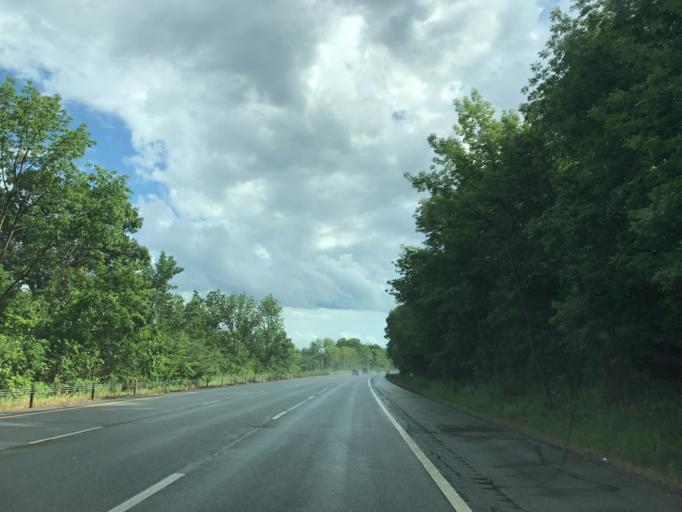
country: US
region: New York
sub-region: Warren County
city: Glens Falls North
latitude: 43.3716
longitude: -73.7017
